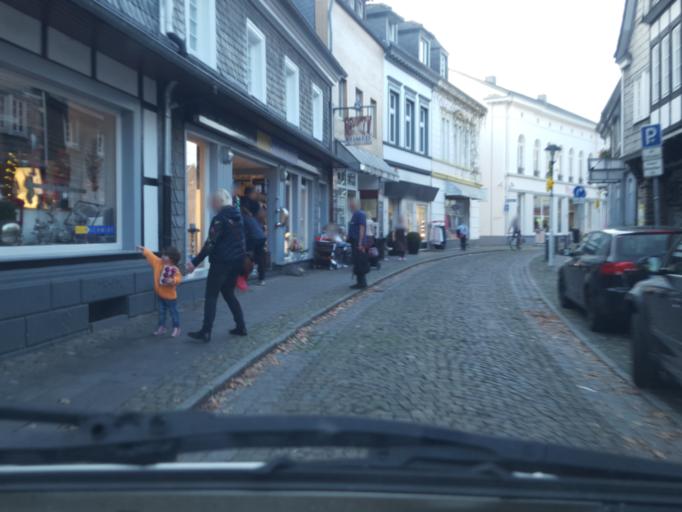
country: DE
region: North Rhine-Westphalia
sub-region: Regierungsbezirk Dusseldorf
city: Heiligenhaus
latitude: 51.3630
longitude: 6.9375
